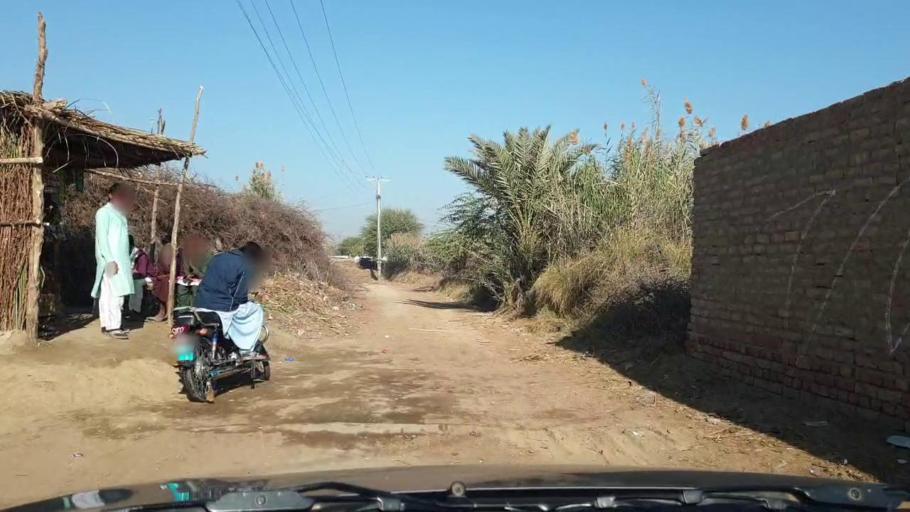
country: PK
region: Sindh
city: Jhol
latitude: 25.9409
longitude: 68.8400
